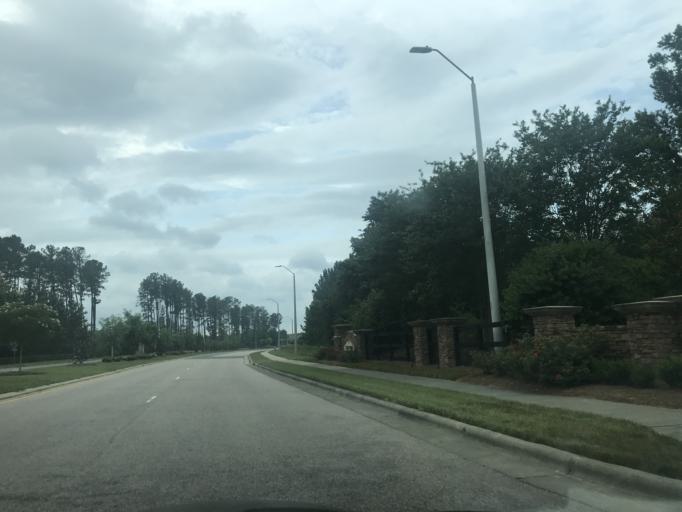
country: US
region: North Carolina
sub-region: Wake County
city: Green Level
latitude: 35.8091
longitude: -78.9030
